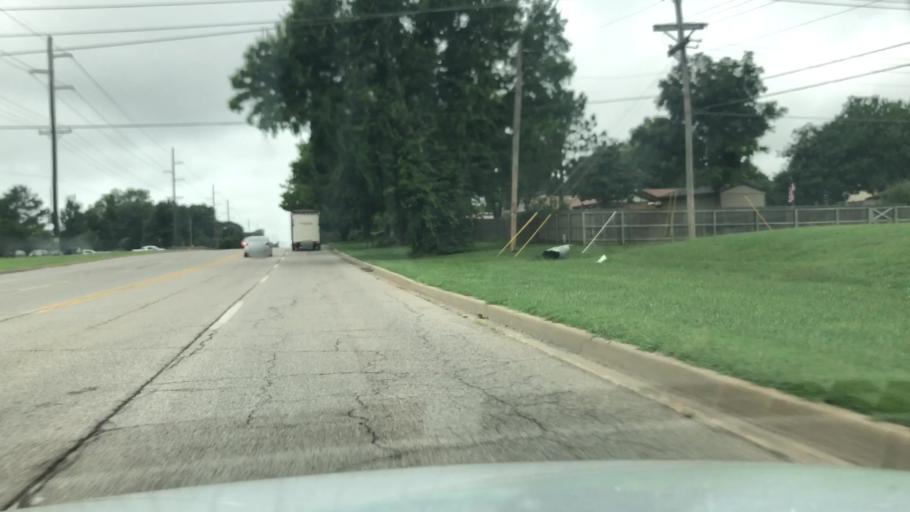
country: US
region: Oklahoma
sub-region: Washington County
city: Dewey
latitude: 36.7281
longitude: -95.9080
